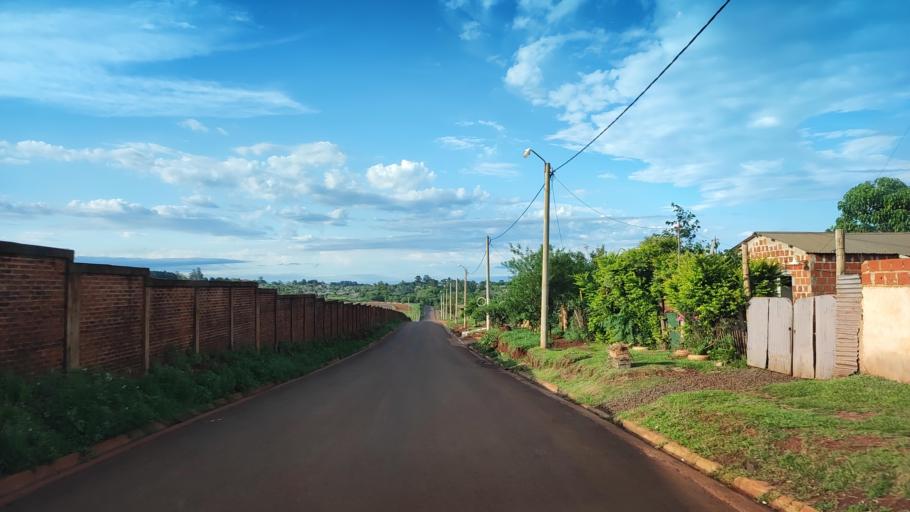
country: AR
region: Misiones
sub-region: Departamento de Capital
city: Posadas
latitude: -27.4421
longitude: -55.9247
